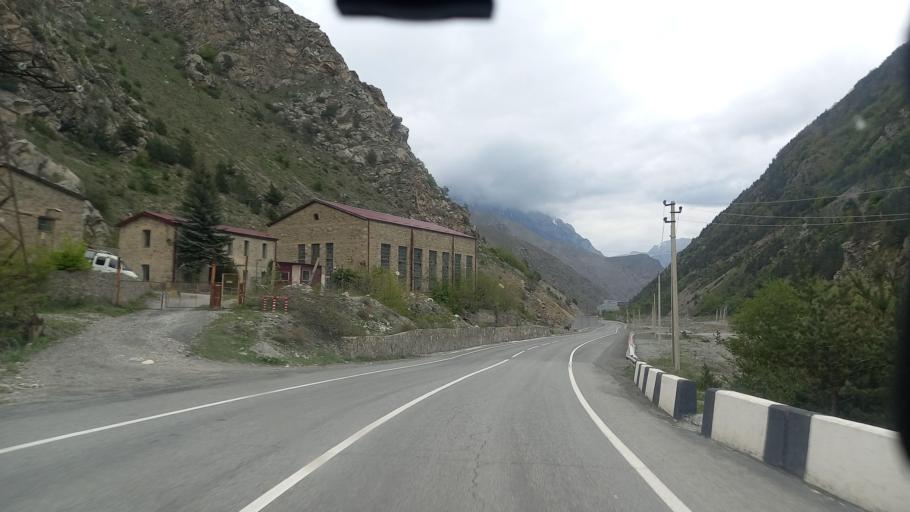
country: RU
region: North Ossetia
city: Mizur
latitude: 42.8391
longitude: 44.0282
